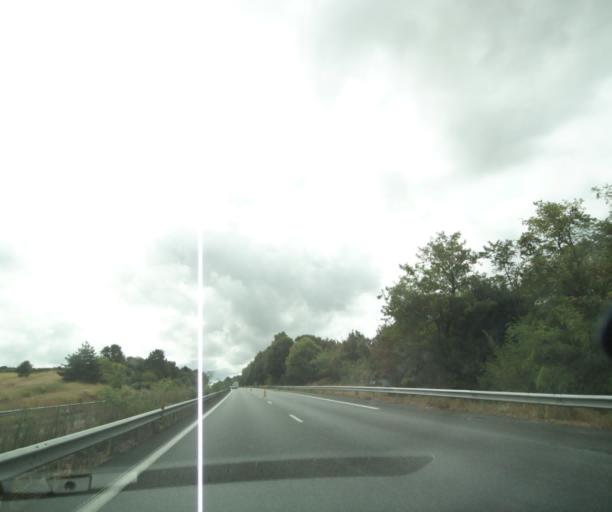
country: FR
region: Poitou-Charentes
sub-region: Departement de la Charente-Maritime
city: Mirambeau
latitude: 45.3574
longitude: -0.5859
